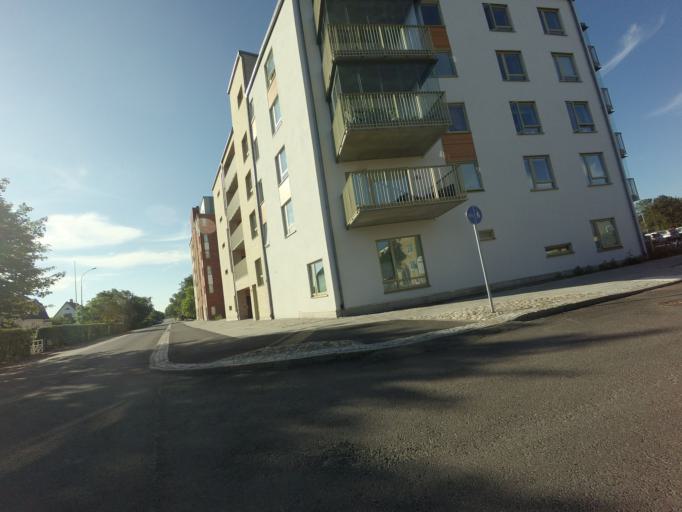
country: SE
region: Skane
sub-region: Hoganas Kommun
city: Hoganas
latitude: 56.1980
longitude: 12.5579
